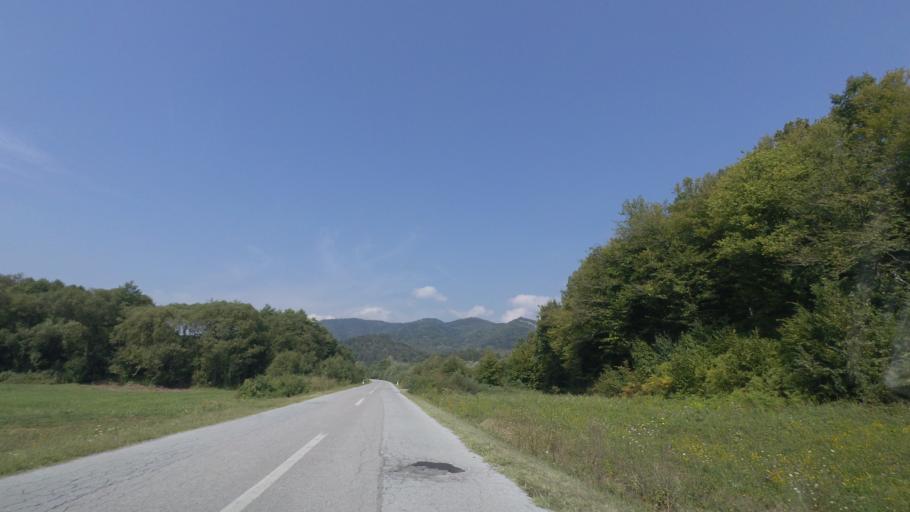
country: HR
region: Sisacko-Moslavacka
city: Dvor
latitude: 45.1371
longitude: 16.2361
